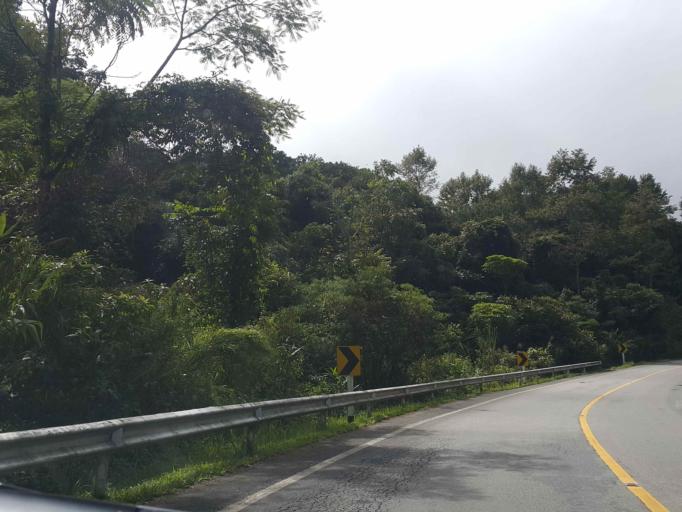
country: TH
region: Chiang Mai
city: Mae Chaem
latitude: 18.5188
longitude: 98.5004
